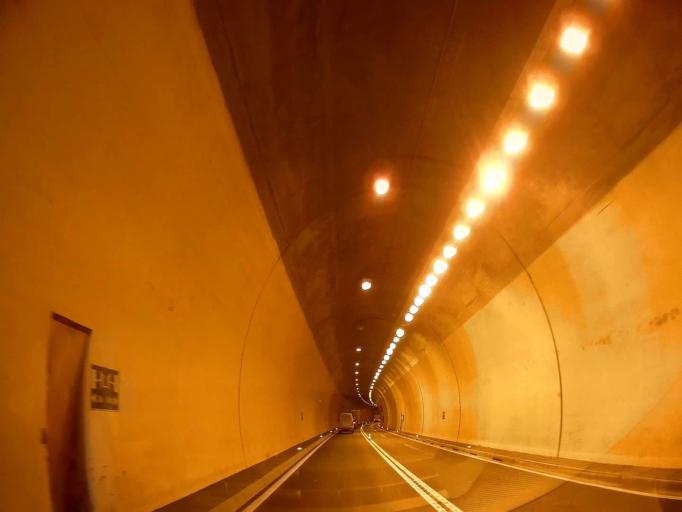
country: AT
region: Carinthia
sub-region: Politischer Bezirk Spittal an der Drau
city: Sachsenburg
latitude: 46.8216
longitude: 13.3539
